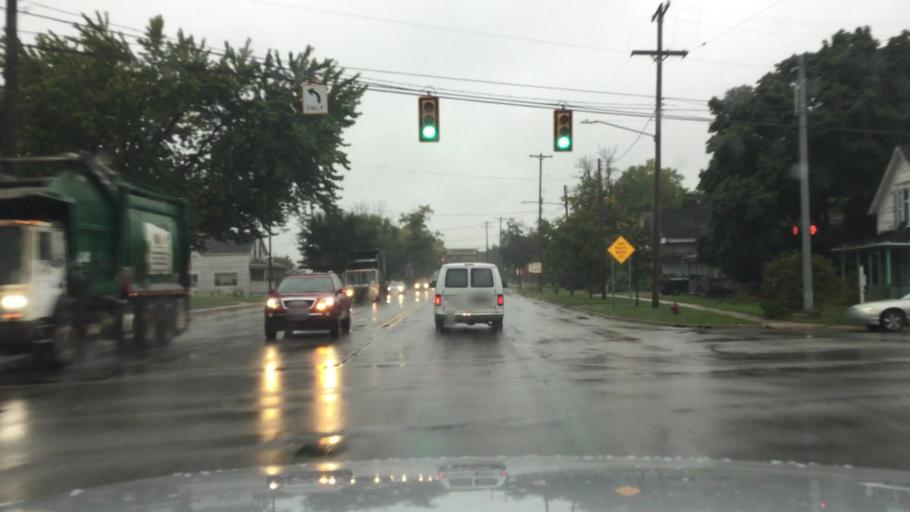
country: US
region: Michigan
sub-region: Saginaw County
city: Saginaw
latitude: 43.4101
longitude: -83.9548
